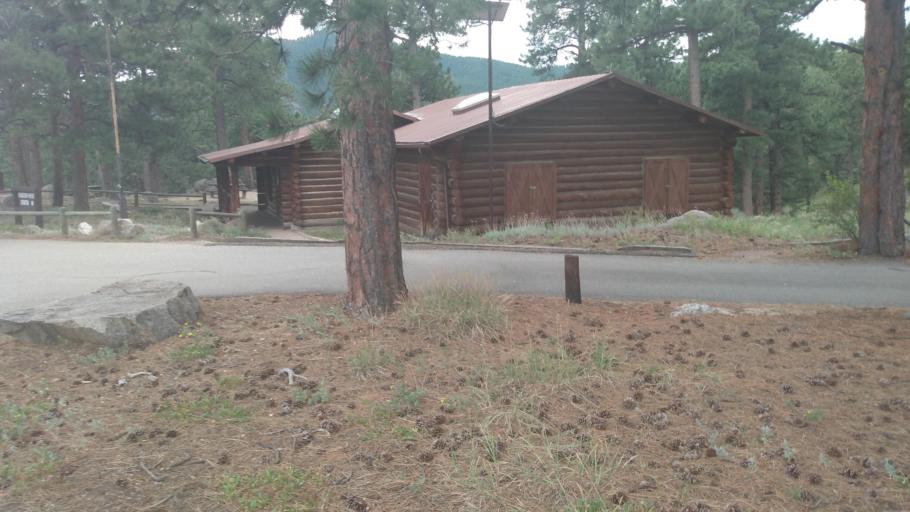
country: US
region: Colorado
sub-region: Boulder County
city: Boulder
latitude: 40.0041
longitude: -105.3033
